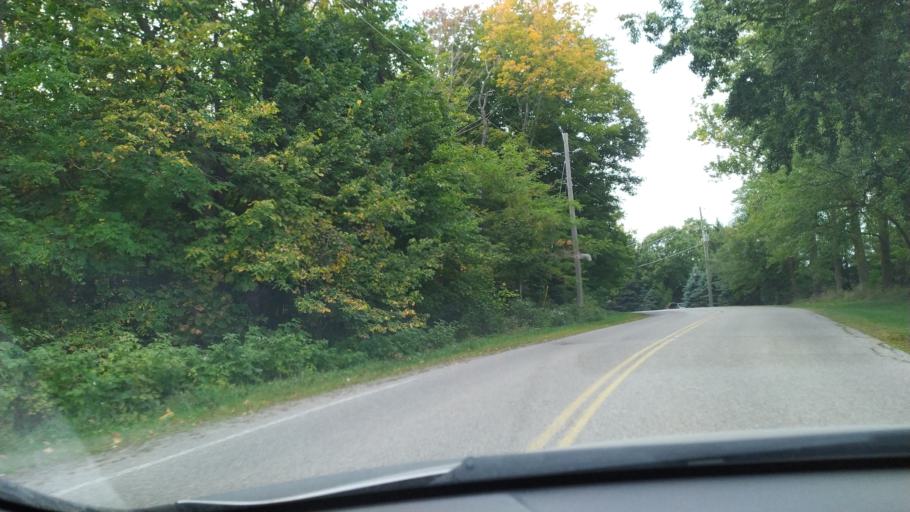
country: CA
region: Ontario
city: Stratford
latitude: 43.4641
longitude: -80.7670
